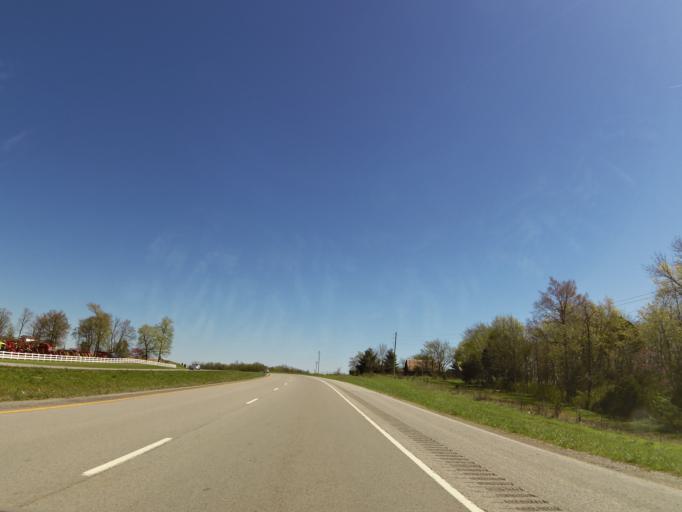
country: US
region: Kentucky
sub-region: Logan County
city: Auburn
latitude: 36.8777
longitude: -86.6710
